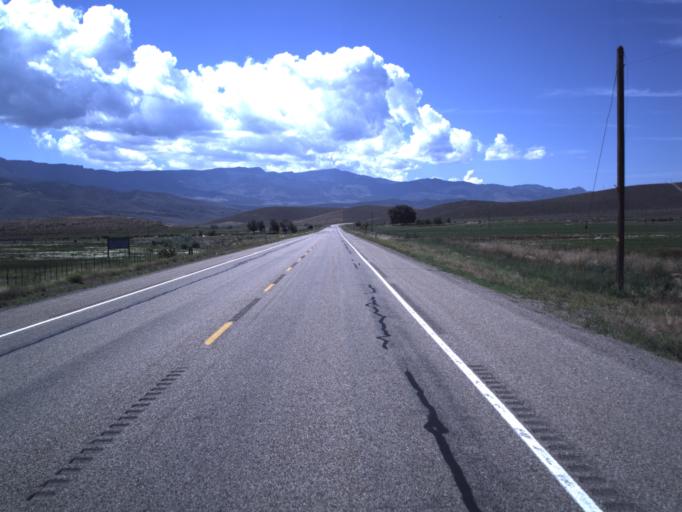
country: US
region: Utah
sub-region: Piute County
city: Junction
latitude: 38.2314
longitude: -112.2199
